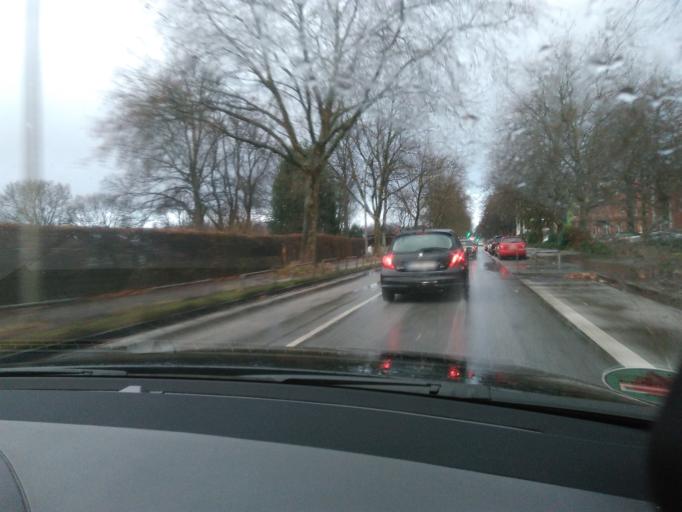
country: DE
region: Hamburg
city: Barmbek-Nord
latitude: 53.6027
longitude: 10.0354
